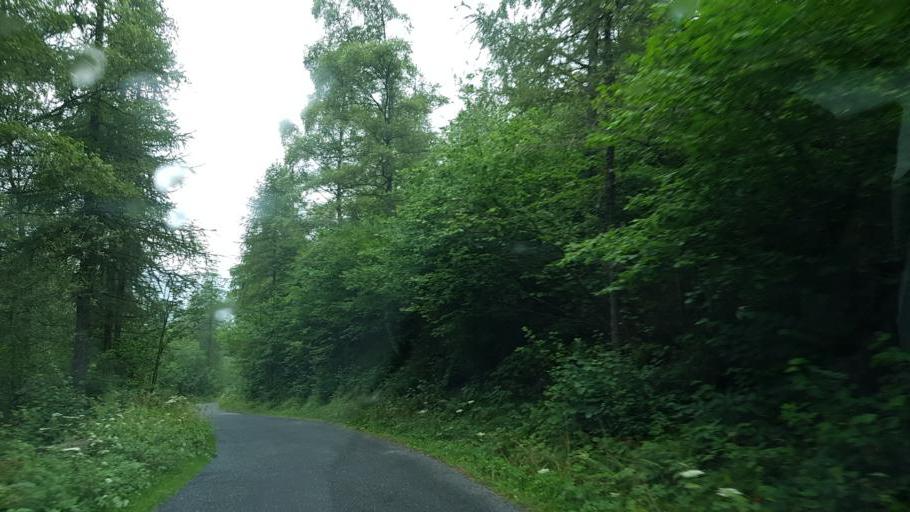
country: IT
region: Piedmont
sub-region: Provincia di Cuneo
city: Sampeyre
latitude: 44.5641
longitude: 7.1757
